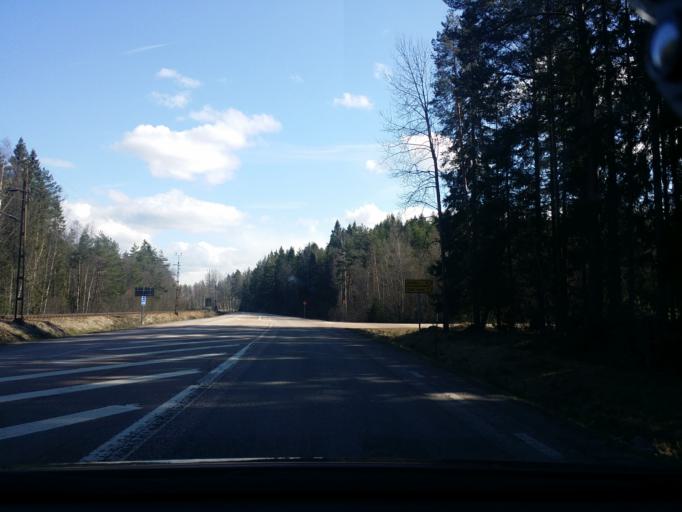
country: SE
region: Vaestmanland
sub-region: Sala Kommun
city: Sala
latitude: 59.9681
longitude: 16.5051
